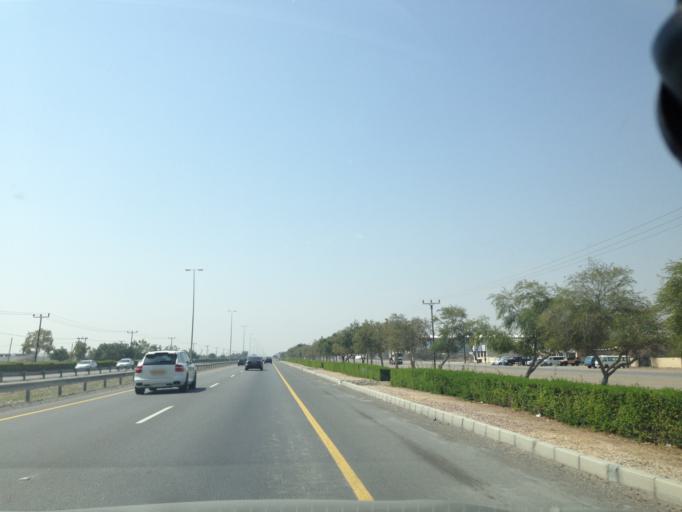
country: OM
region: Al Batinah
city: Barka'
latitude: 23.6721
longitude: 57.9798
